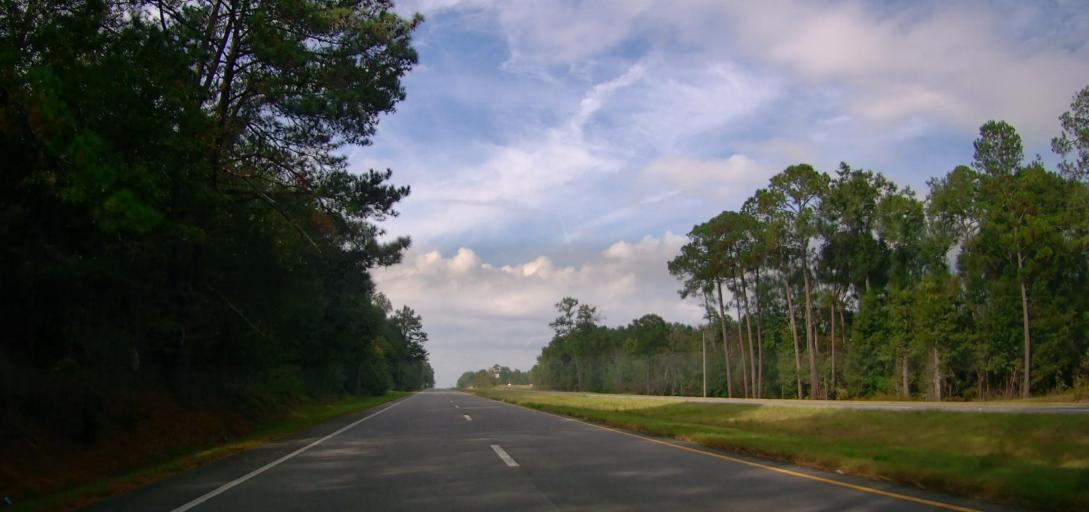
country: US
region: Georgia
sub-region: Thomas County
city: Meigs
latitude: 30.9711
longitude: -84.0343
